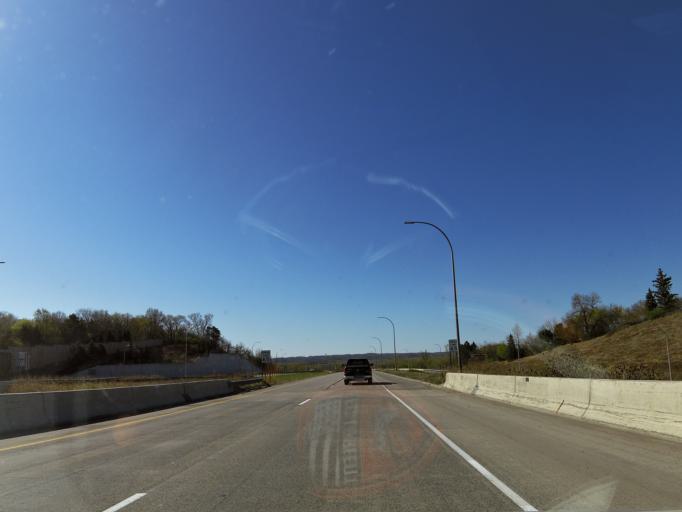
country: US
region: Minnesota
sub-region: Scott County
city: Savage
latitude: 44.8083
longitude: -93.3987
